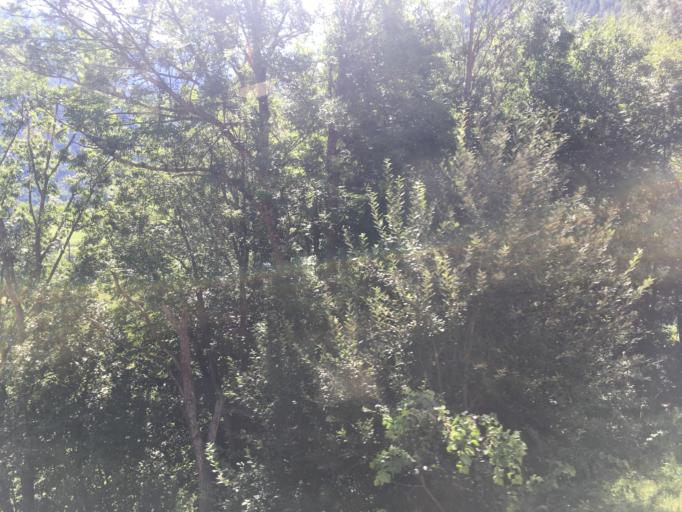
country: CH
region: Valais
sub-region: Visp District
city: Stalden
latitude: 46.2278
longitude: 7.8598
